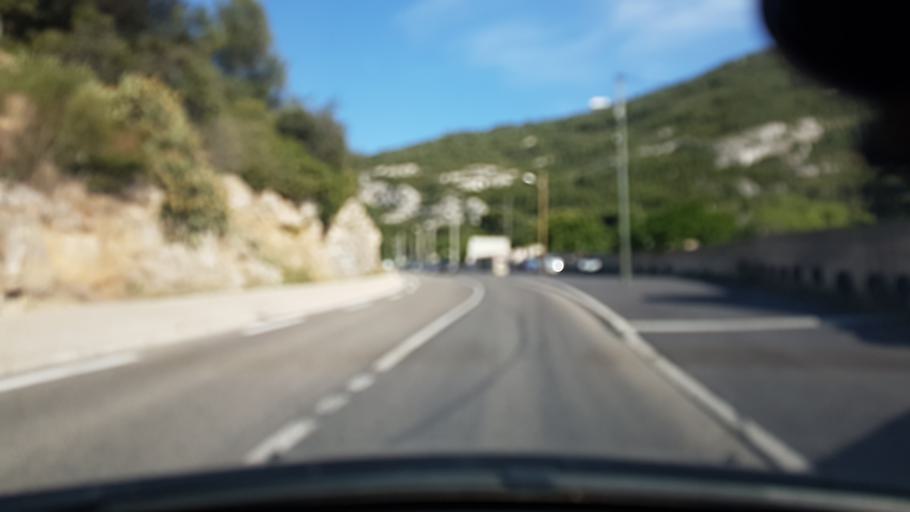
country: FR
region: Provence-Alpes-Cote d'Azur
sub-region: Departement des Bouches-du-Rhone
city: Marseille 11
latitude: 43.2486
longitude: 5.4536
